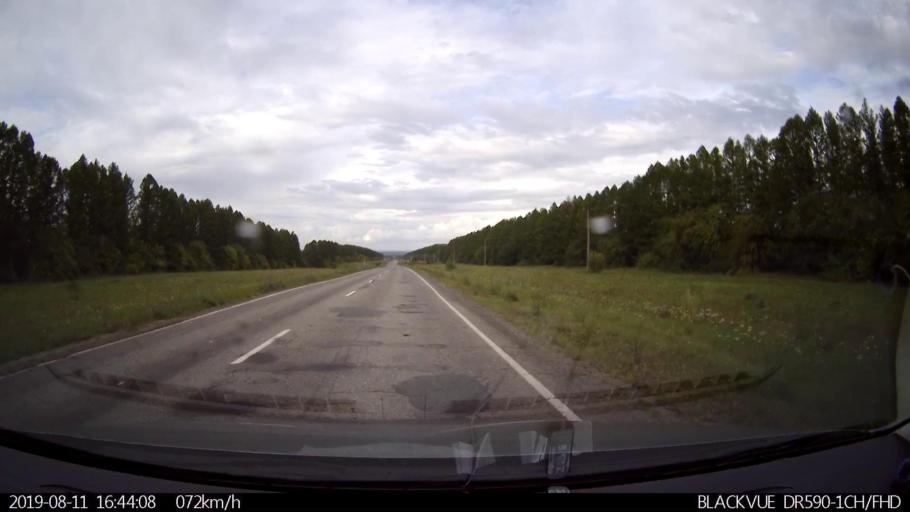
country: RU
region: Ulyanovsk
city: Mayna
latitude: 54.1761
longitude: 47.6782
